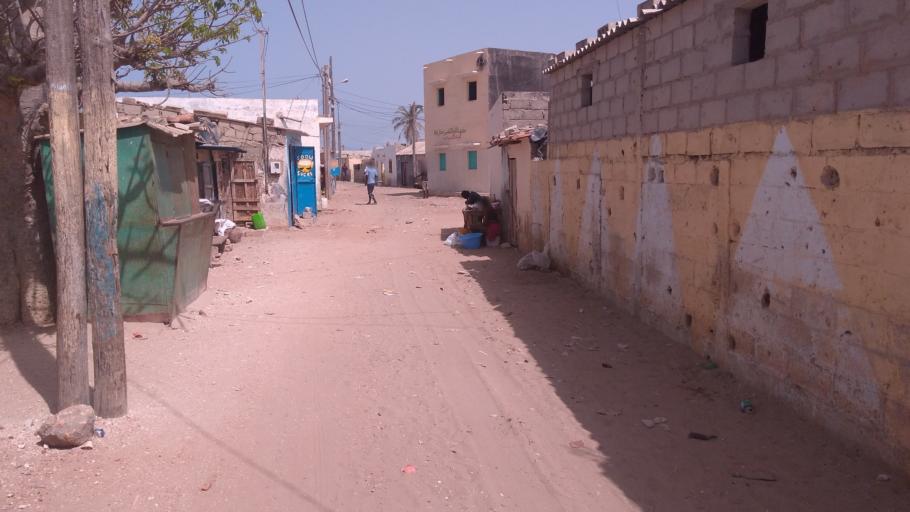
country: SN
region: Dakar
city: Pikine
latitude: 14.6874
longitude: -17.2286
